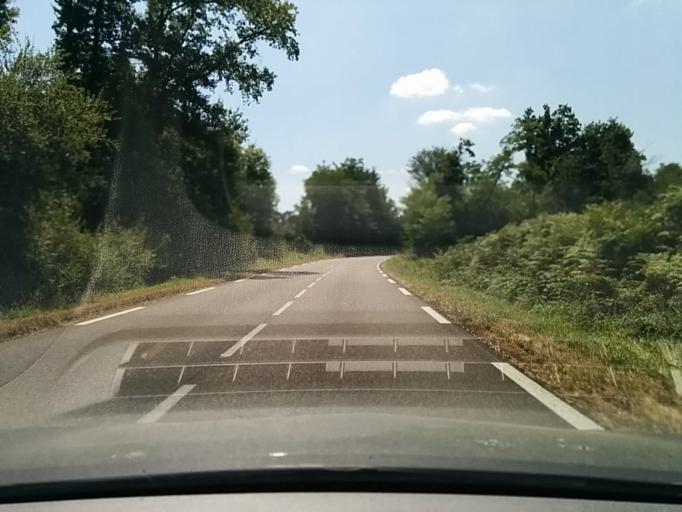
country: FR
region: Midi-Pyrenees
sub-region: Departement du Gers
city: Nogaro
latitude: 43.7915
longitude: 0.0186
